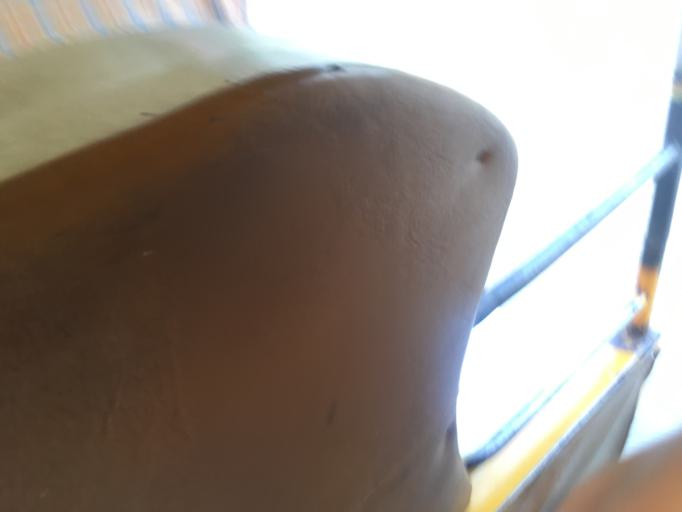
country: IN
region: Telangana
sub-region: Medak
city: Serilingampalle
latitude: 17.4292
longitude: 78.3324
